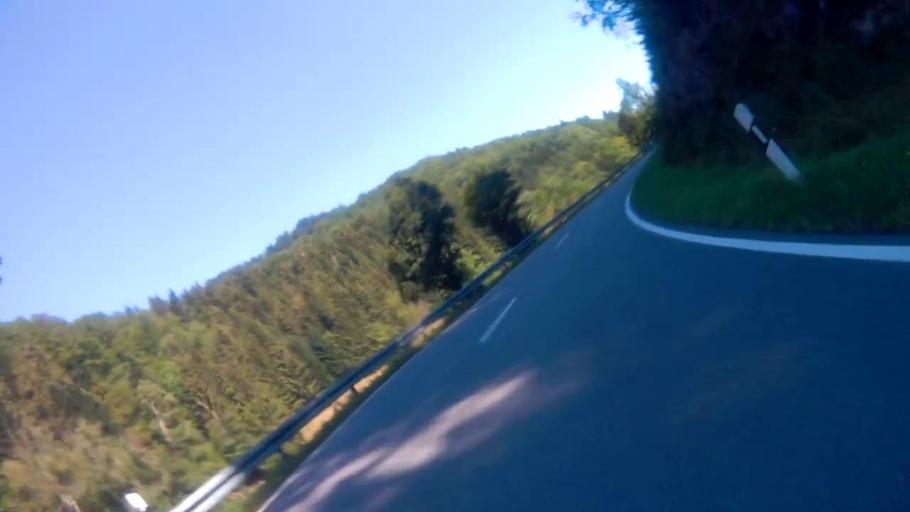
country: DE
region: Baden-Wuerttemberg
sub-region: Freiburg Region
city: Maulburg
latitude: 47.7366
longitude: 7.7652
